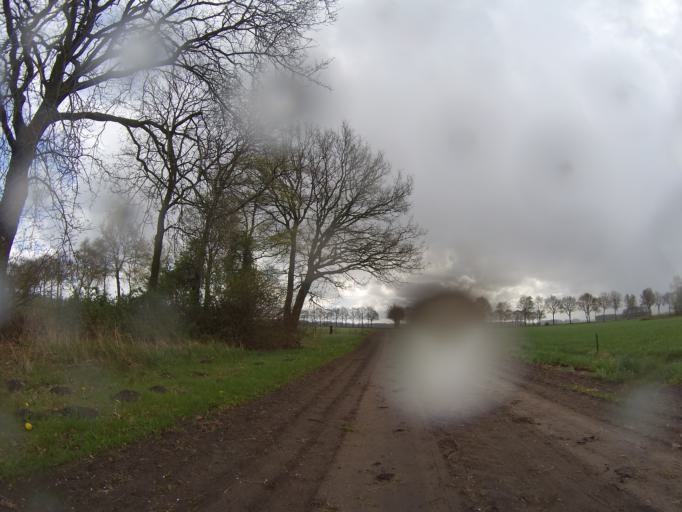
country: NL
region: Drenthe
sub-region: Gemeente Coevorden
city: Dalen
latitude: 52.7647
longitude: 6.6968
